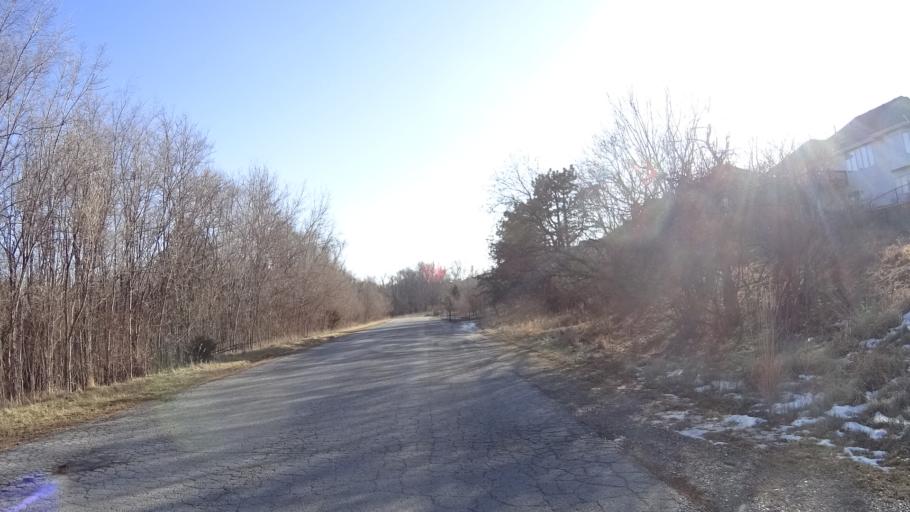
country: US
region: Nebraska
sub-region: Douglas County
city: Bennington
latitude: 41.3097
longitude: -96.1314
